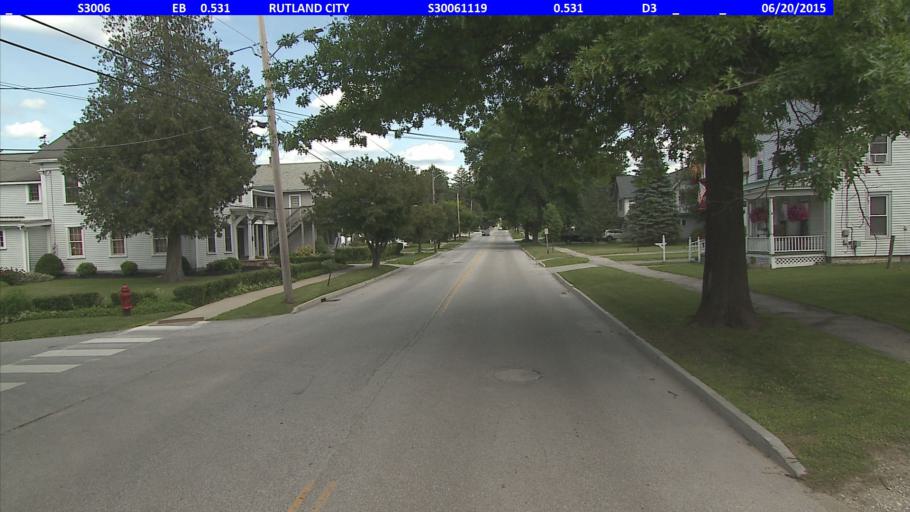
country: US
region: Vermont
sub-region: Rutland County
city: Rutland
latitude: 43.6156
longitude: -72.9813
